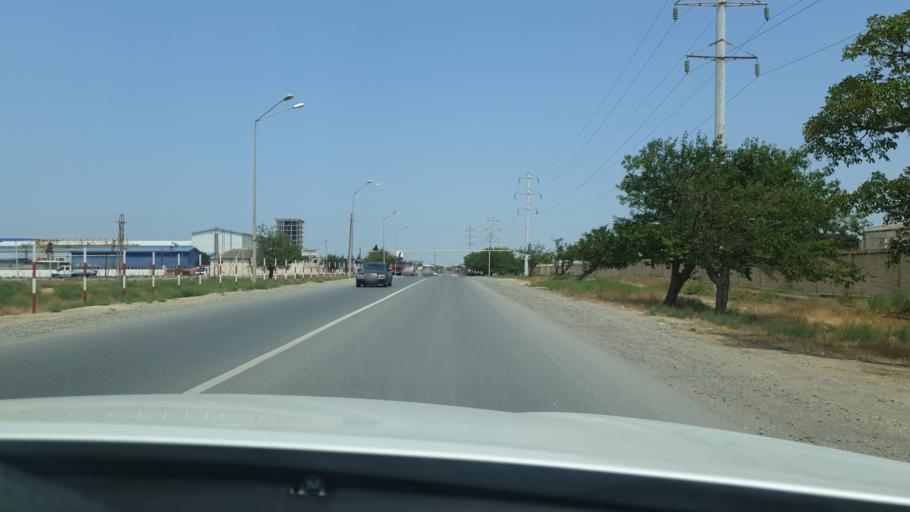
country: AZ
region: Baki
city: Qaracuxur
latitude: 40.3973
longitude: 49.9994
